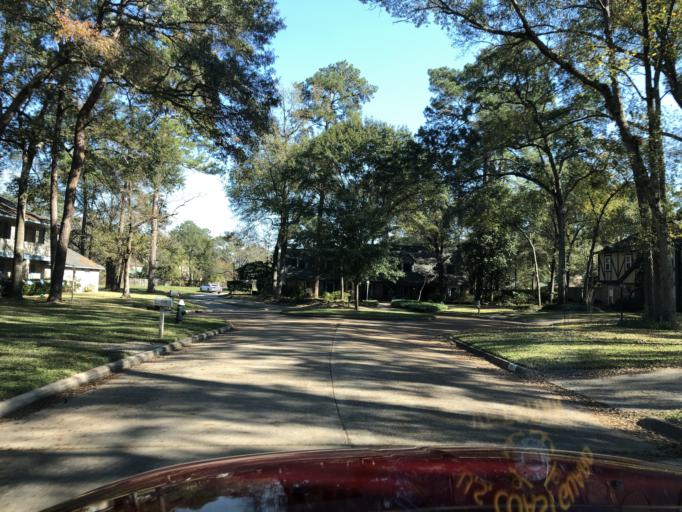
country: US
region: Texas
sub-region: Harris County
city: Tomball
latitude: 30.0299
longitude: -95.5396
